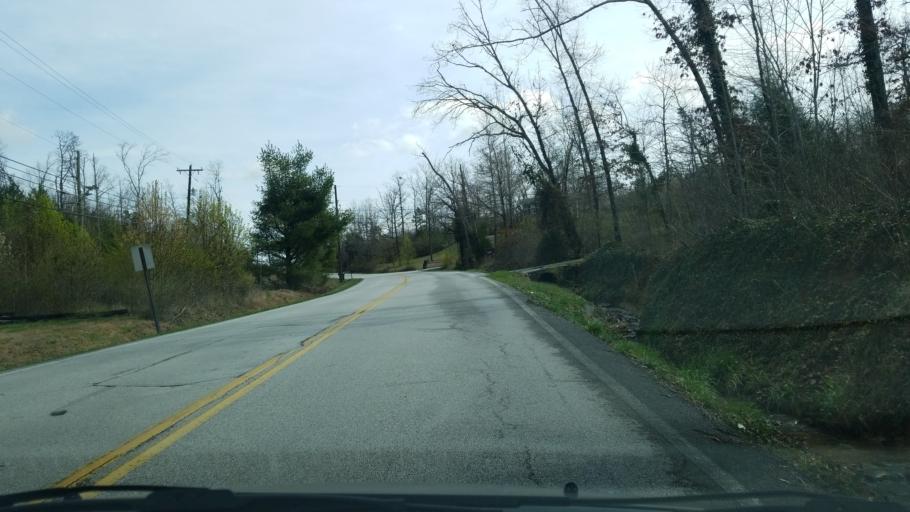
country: US
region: Tennessee
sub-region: Hamilton County
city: Harrison
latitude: 35.1390
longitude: -85.1089
